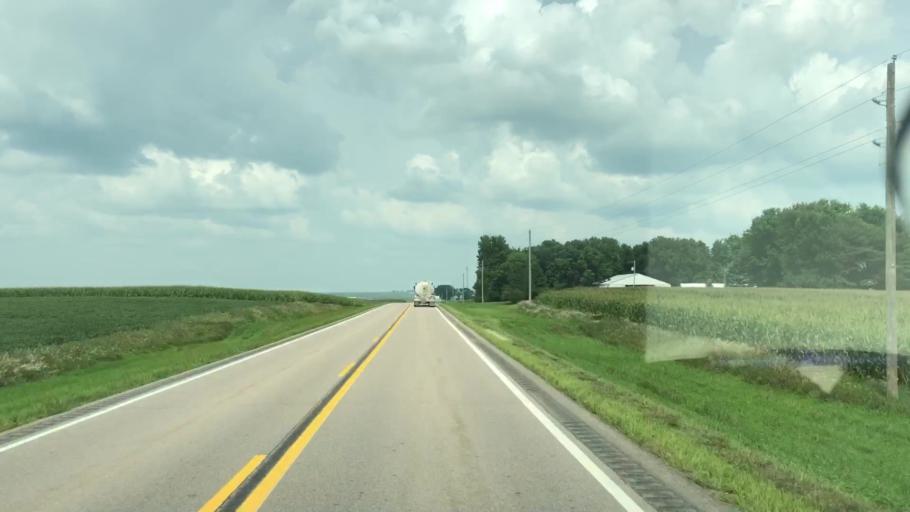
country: US
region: Iowa
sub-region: Plymouth County
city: Remsen
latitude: 42.7961
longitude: -95.9577
